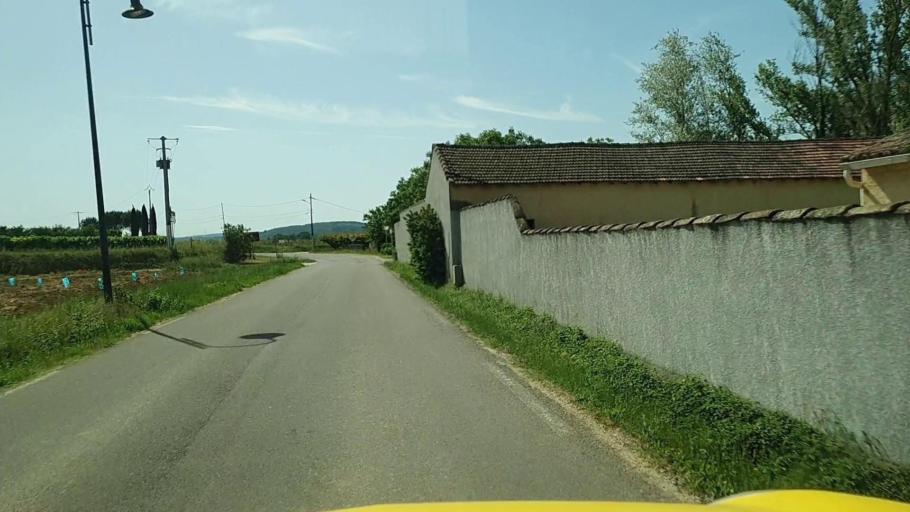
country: FR
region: Languedoc-Roussillon
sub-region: Departement du Gard
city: Sabran
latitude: 44.1108
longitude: 4.5273
